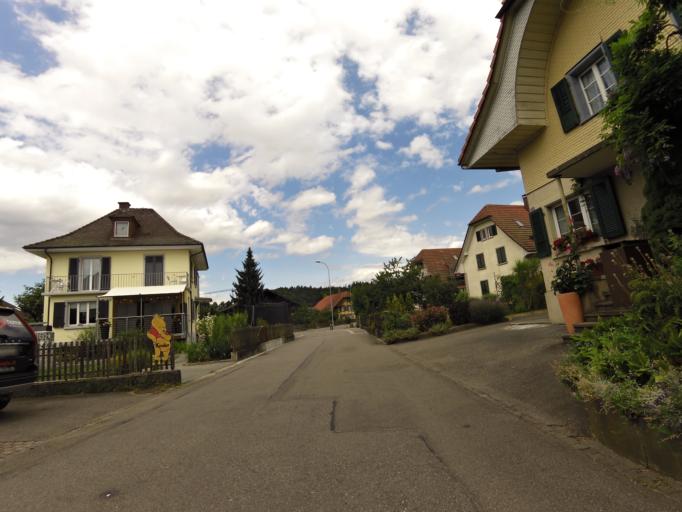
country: CH
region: Bern
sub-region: Oberaargau
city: Aarwangen
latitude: 47.2353
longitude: 7.7811
